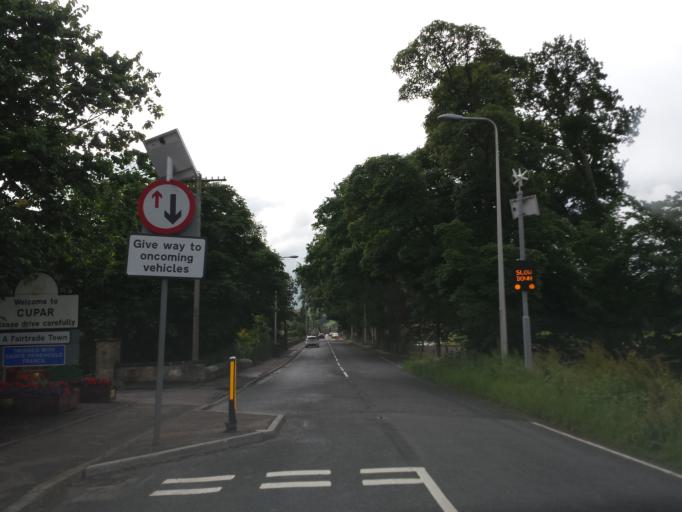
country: GB
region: Scotland
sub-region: Fife
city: Cupar
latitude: 56.3227
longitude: -3.0288
